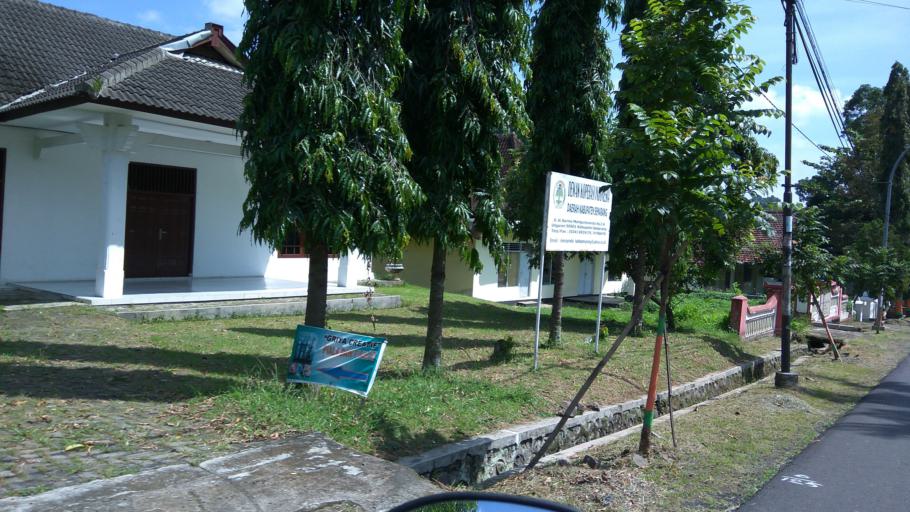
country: ID
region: Central Java
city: Ungaran
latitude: -7.1189
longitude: 110.4049
